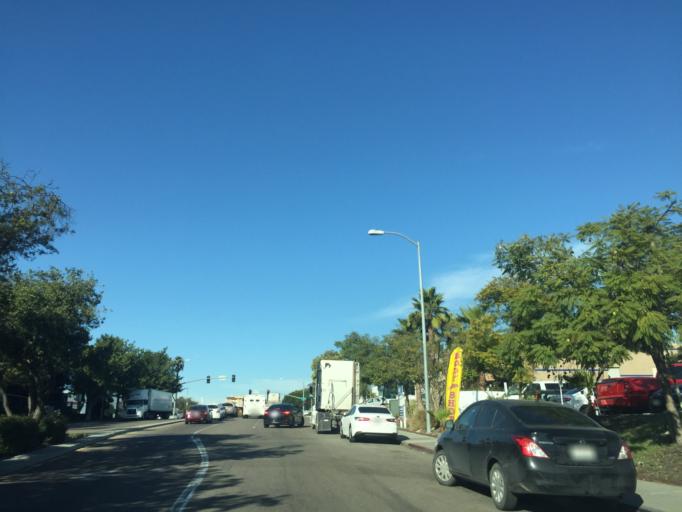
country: MX
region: Baja California
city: Tijuana
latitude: 32.5556
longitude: -116.9359
